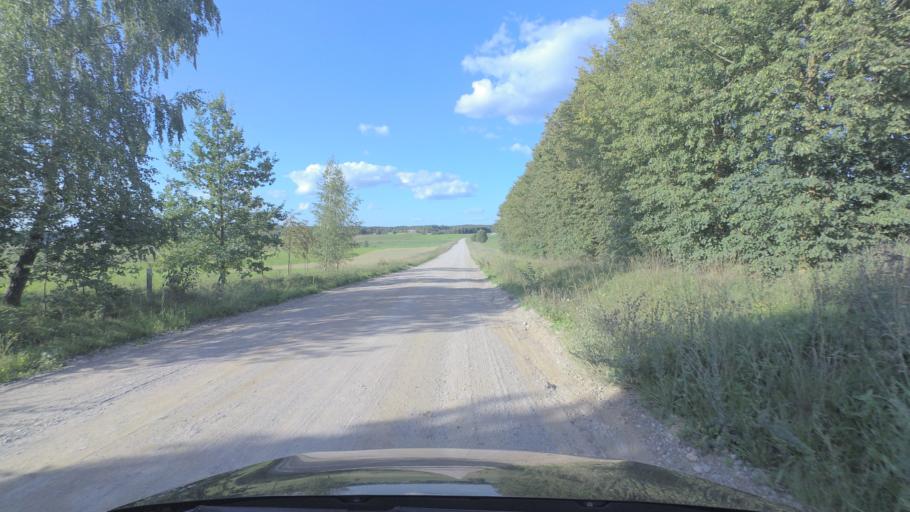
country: LT
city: Pabrade
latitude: 55.1301
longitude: 25.7057
